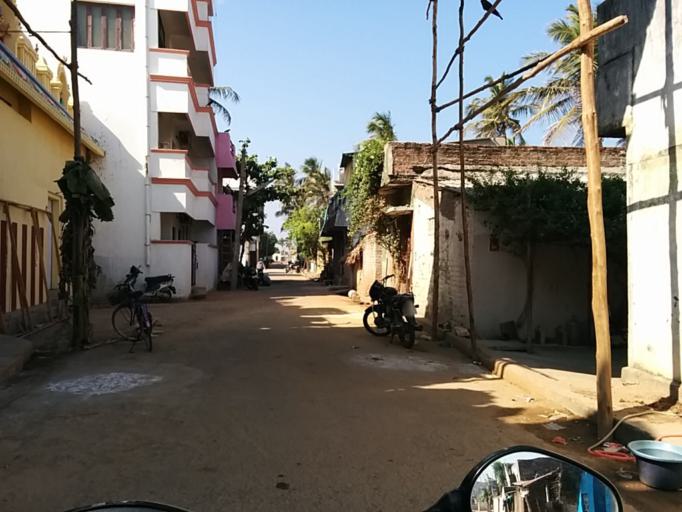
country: IN
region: Pondicherry
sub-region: Puducherry
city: Puducherry
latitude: 11.9452
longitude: 79.8375
